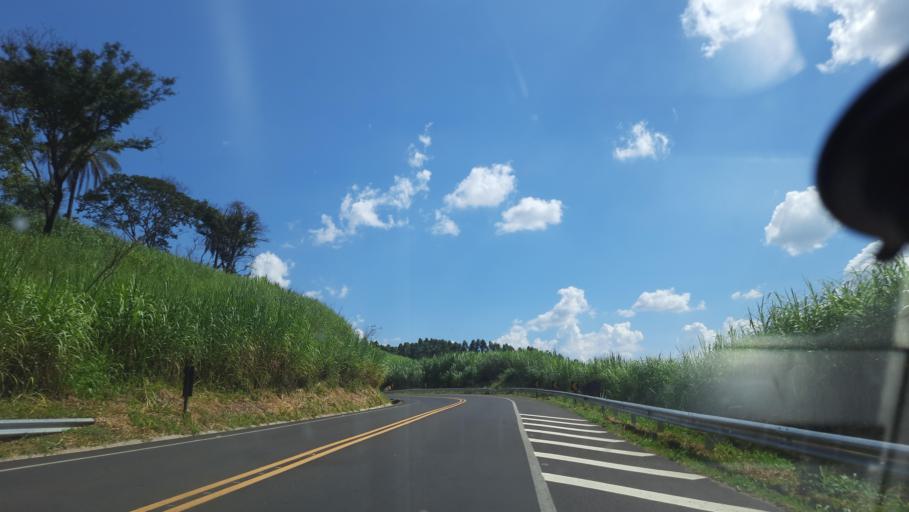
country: BR
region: Sao Paulo
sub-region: Sao Jose Do Rio Pardo
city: Sao Jose do Rio Pardo
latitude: -21.6019
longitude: -46.9377
